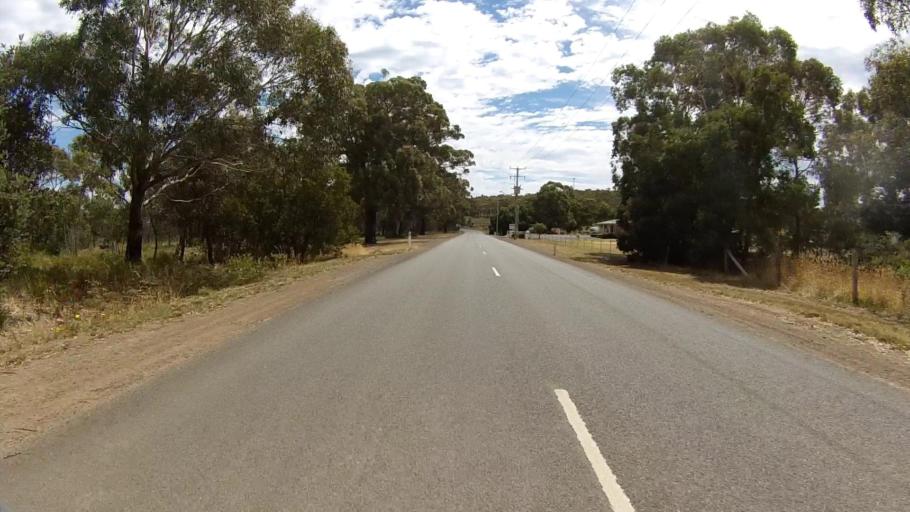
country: AU
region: Tasmania
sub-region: Sorell
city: Sorell
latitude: -42.8874
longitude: 147.6695
